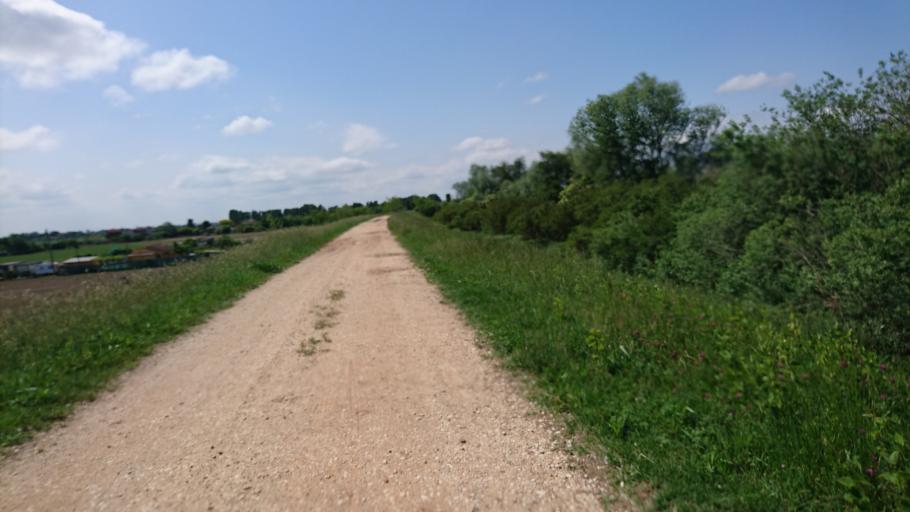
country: IT
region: Veneto
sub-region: Provincia di Padova
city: Codevigo
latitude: 45.2466
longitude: 12.1154
